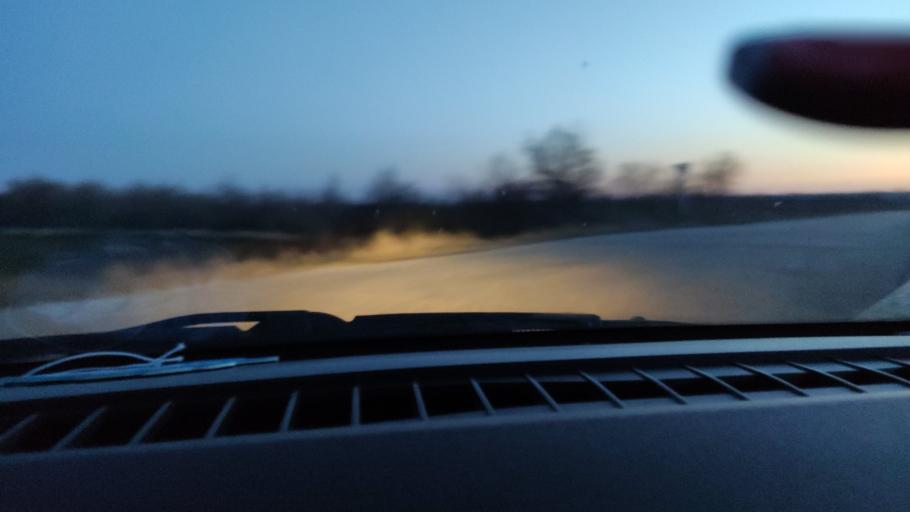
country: RU
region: Saratov
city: Rovnoye
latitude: 50.9412
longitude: 46.1279
